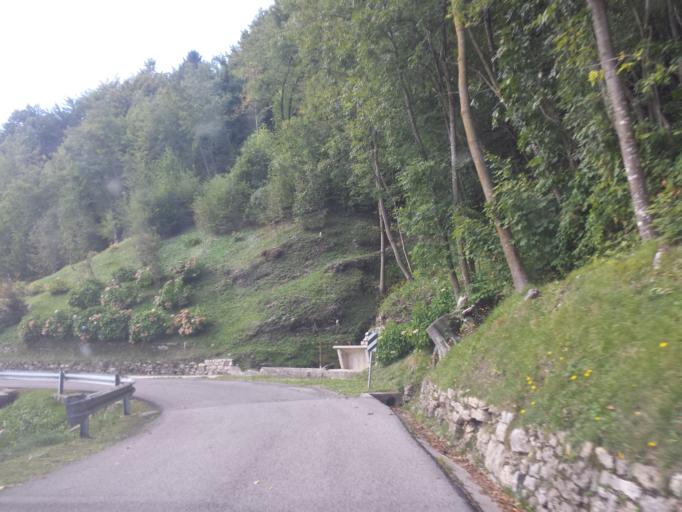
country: IT
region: Veneto
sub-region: Provincia di Vicenza
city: Recoaro Terme
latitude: 45.7154
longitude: 11.1841
